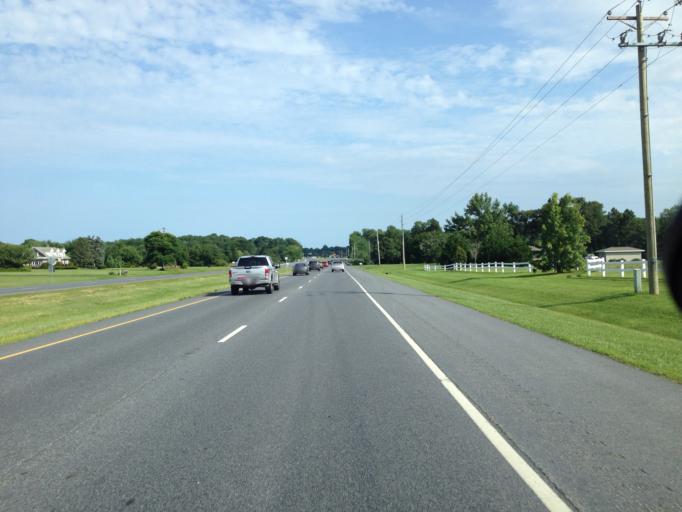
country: US
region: Delaware
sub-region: Sussex County
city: Milton
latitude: 38.8273
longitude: -75.3114
